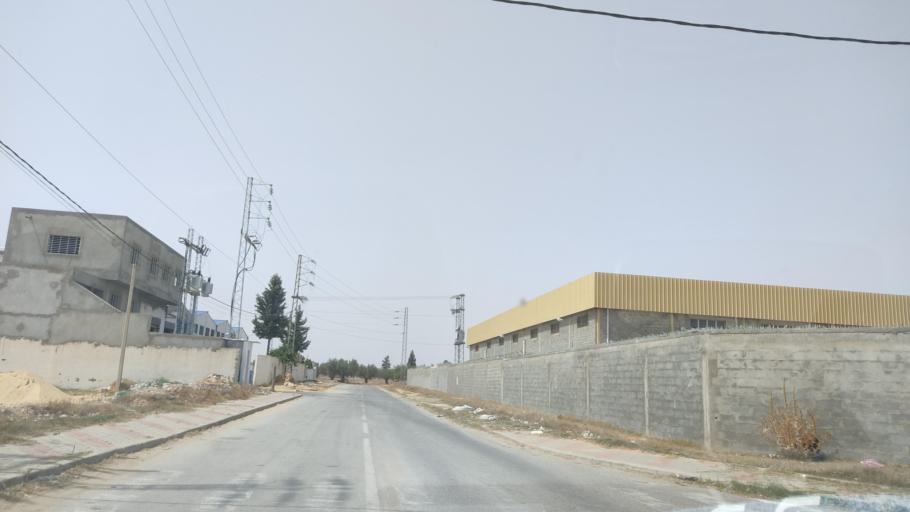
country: TN
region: Al Mahdiyah
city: El Jem
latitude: 35.1288
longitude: 10.7370
